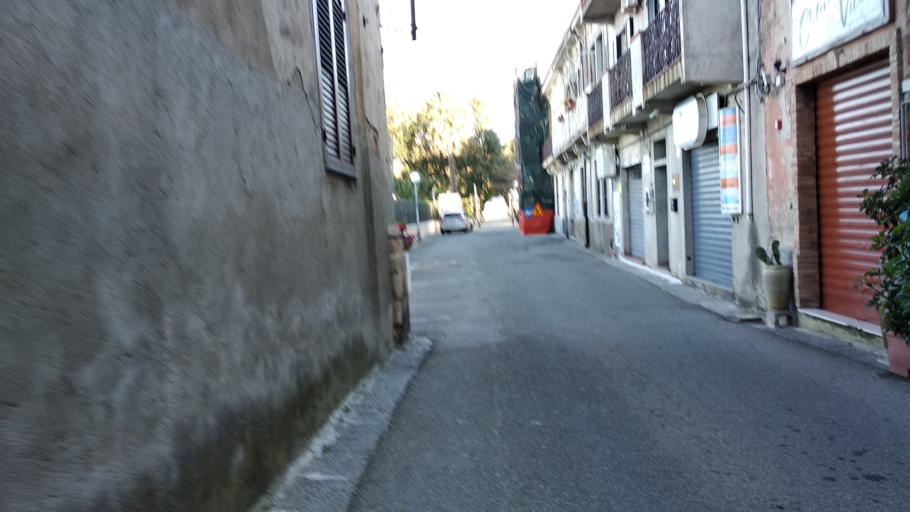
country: IT
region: Calabria
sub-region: Provincia di Reggio Calabria
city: Seminara
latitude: 38.3559
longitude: 15.8446
